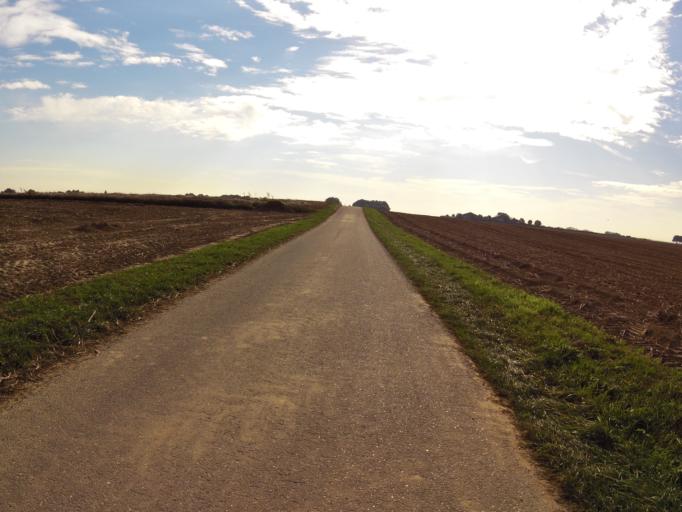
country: NL
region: Limburg
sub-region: Gemeente Schinnen
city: Puth
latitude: 50.9653
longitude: 5.8878
